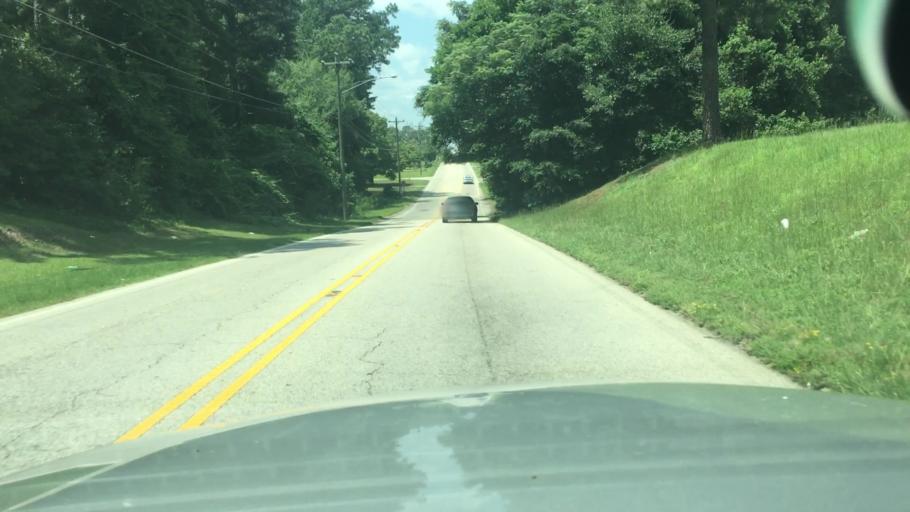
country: US
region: North Carolina
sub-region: Cumberland County
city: Fayetteville
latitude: 35.0220
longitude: -78.9036
